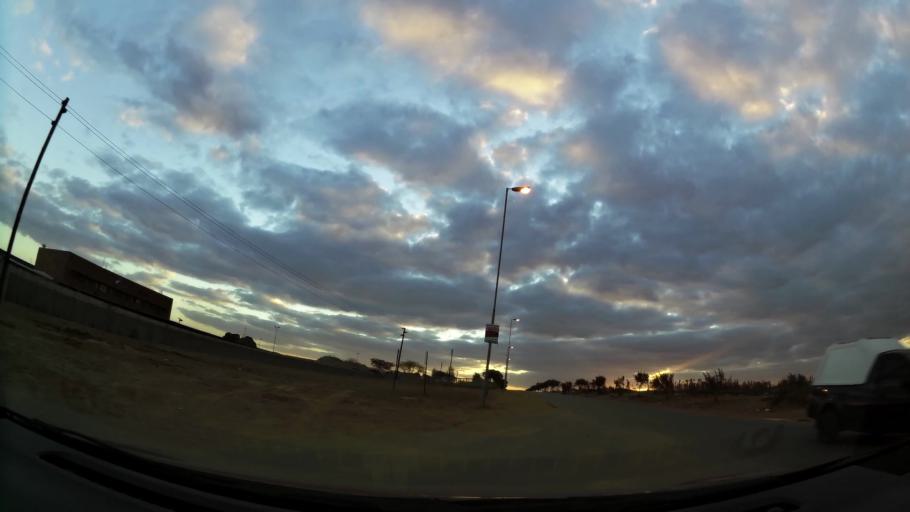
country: ZA
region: Gauteng
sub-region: City of Johannesburg Metropolitan Municipality
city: Midrand
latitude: -25.9802
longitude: 28.1714
